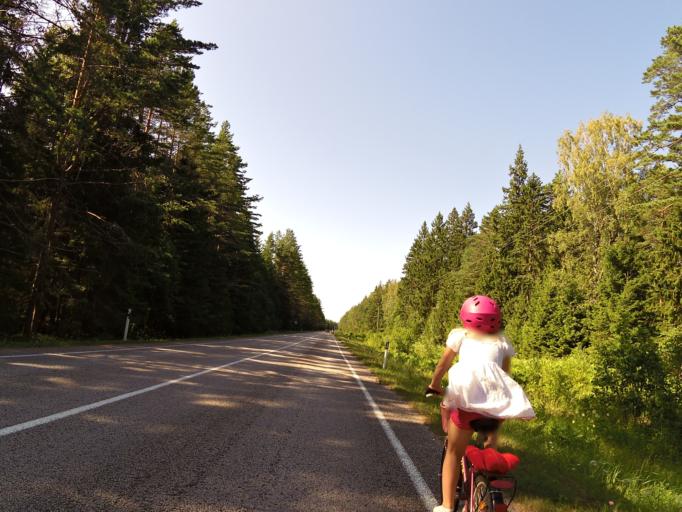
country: EE
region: Hiiumaa
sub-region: Kaerdla linn
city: Kardla
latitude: 58.8636
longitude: 22.4632
